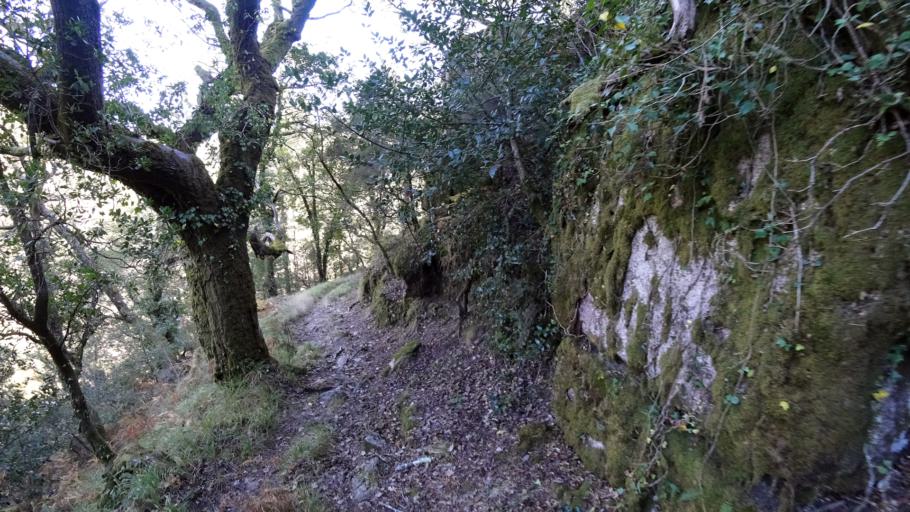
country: ES
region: Galicia
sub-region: Provincia de Ourense
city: Lobios
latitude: 41.7968
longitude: -8.1514
